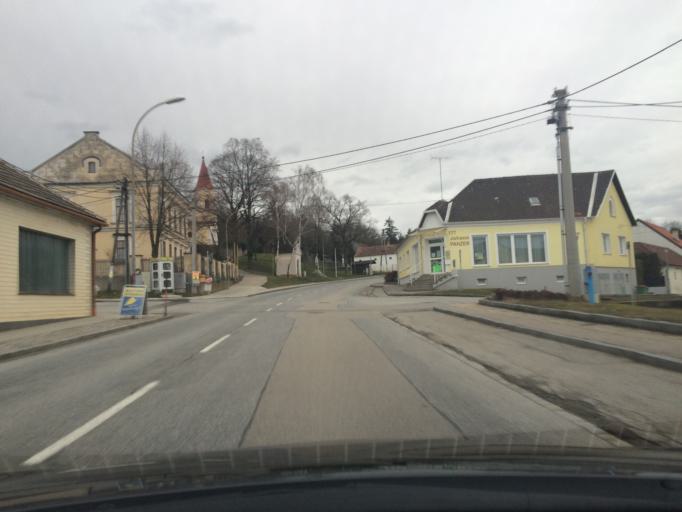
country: AT
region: Lower Austria
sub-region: Politischer Bezirk Ganserndorf
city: Zistersdorf
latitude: 48.5724
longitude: 16.7009
